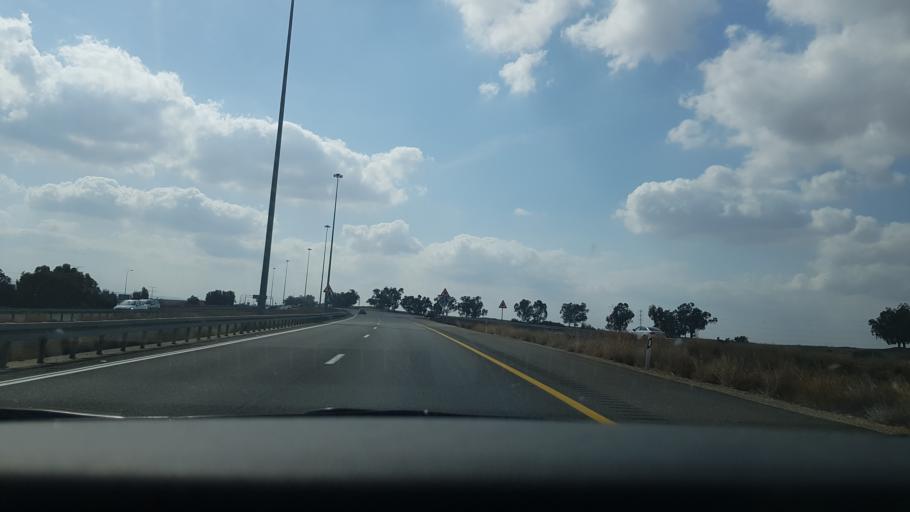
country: IL
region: Southern District
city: Qiryat Gat
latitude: 31.5123
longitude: 34.7818
